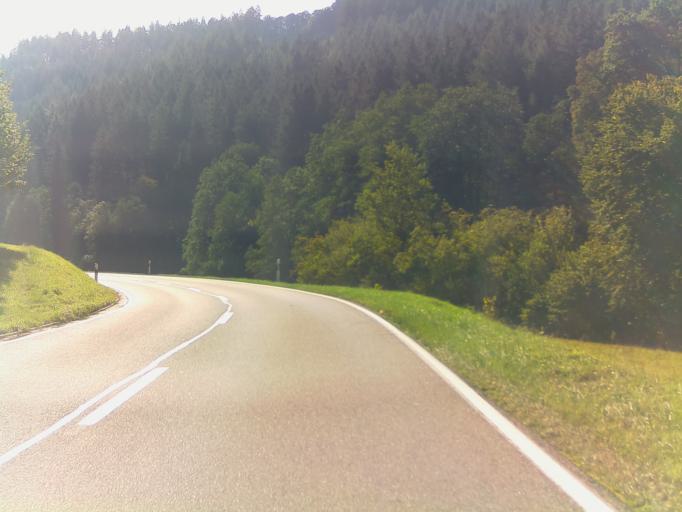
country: DE
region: Baden-Wuerttemberg
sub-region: Karlsruhe Region
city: Heddesbach
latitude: 49.4674
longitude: 8.8571
